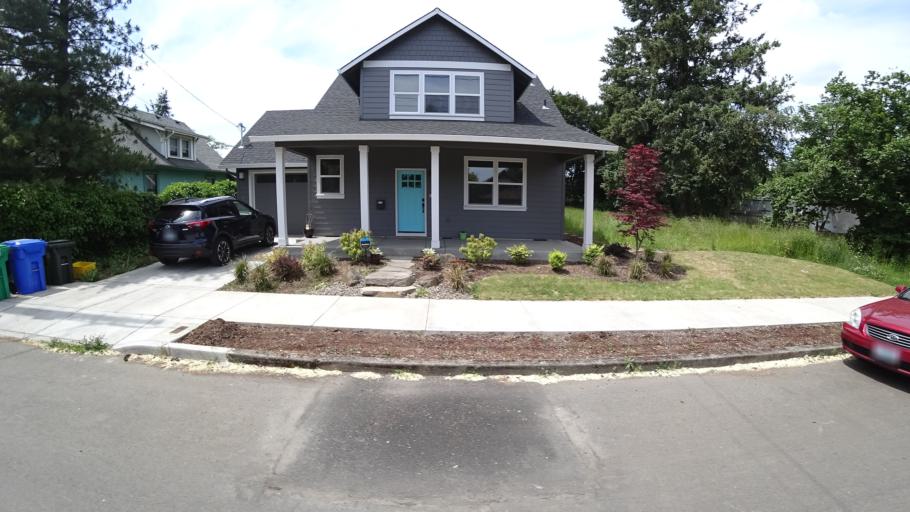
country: US
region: Oregon
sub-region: Multnomah County
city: Lents
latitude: 45.4729
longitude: -122.5923
